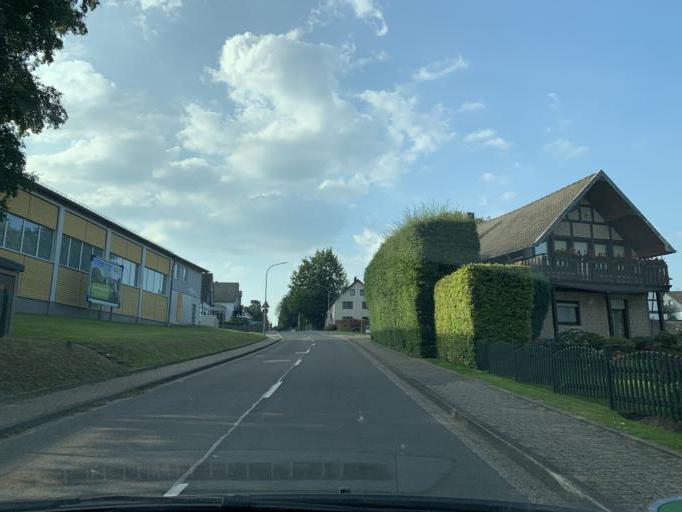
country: DE
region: North Rhine-Westphalia
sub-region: Regierungsbezirk Koln
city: Simmerath
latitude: 50.6256
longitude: 6.3551
